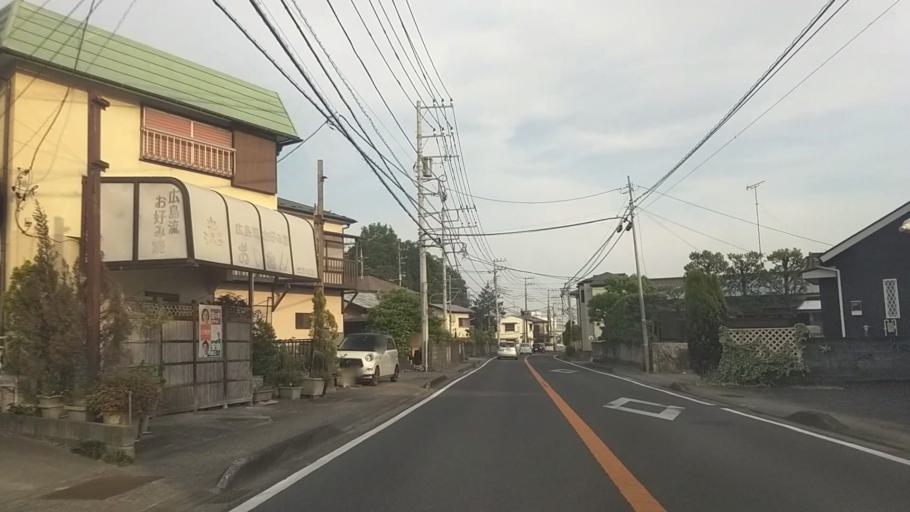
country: JP
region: Kanagawa
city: Odawara
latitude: 35.3087
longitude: 139.1221
